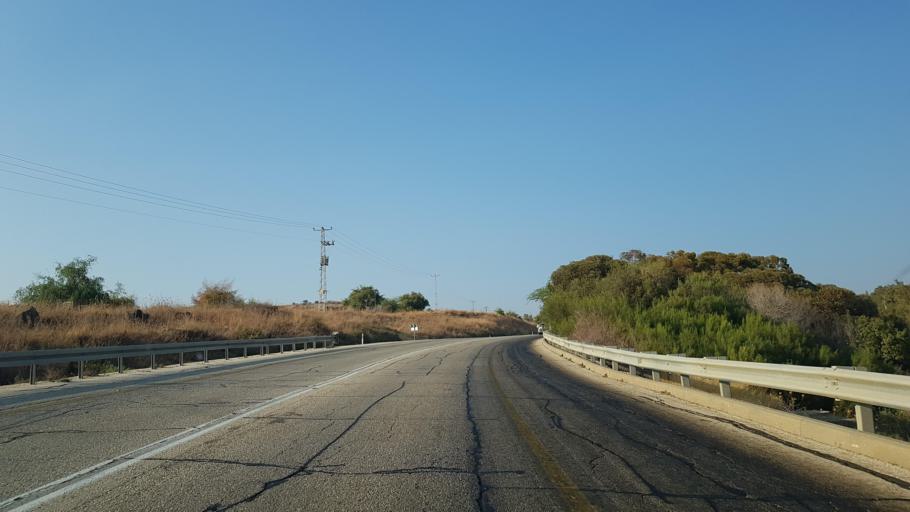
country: SY
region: Quneitra
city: Al Butayhah
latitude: 32.9069
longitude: 35.5971
